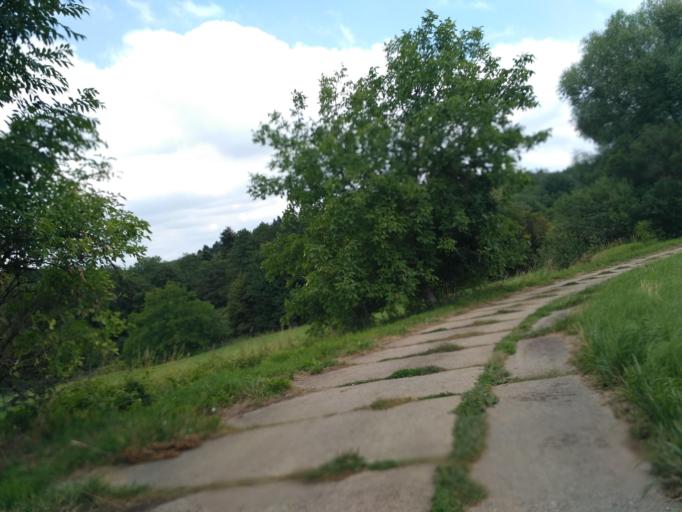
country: PL
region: Subcarpathian Voivodeship
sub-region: Powiat krosnienski
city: Iwonicz-Zdroj
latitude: 49.5693
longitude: 21.8024
